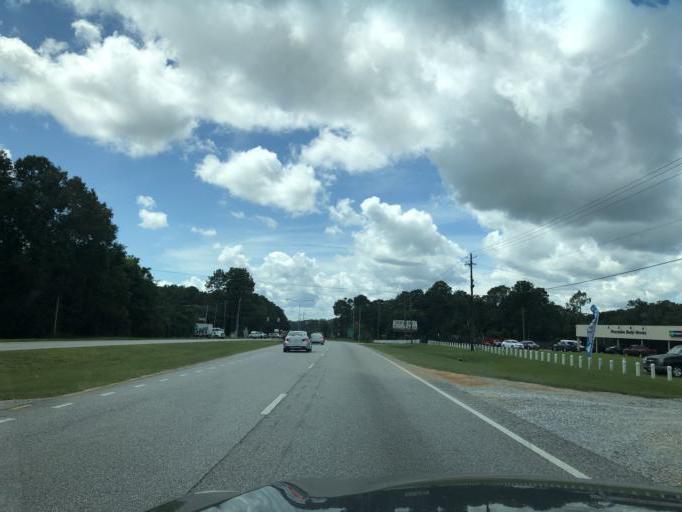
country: US
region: Alabama
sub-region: Barbour County
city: Eufaula
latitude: 31.9186
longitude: -85.1474
